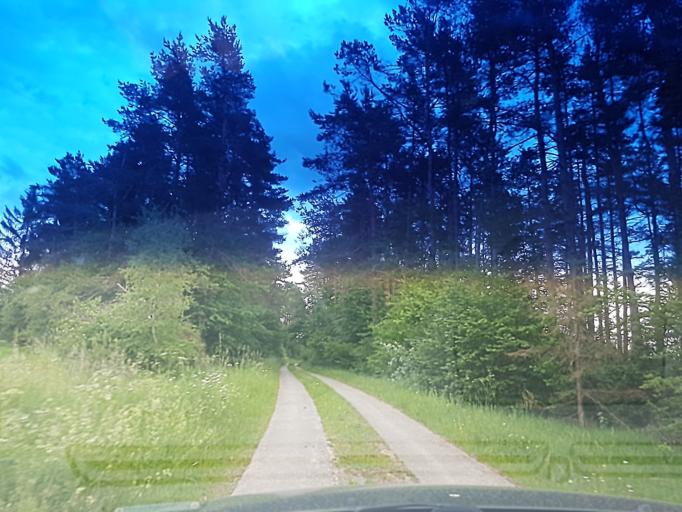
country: DE
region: Bavaria
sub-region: Upper Franconia
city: Wattendorf
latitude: 50.0147
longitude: 11.1151
